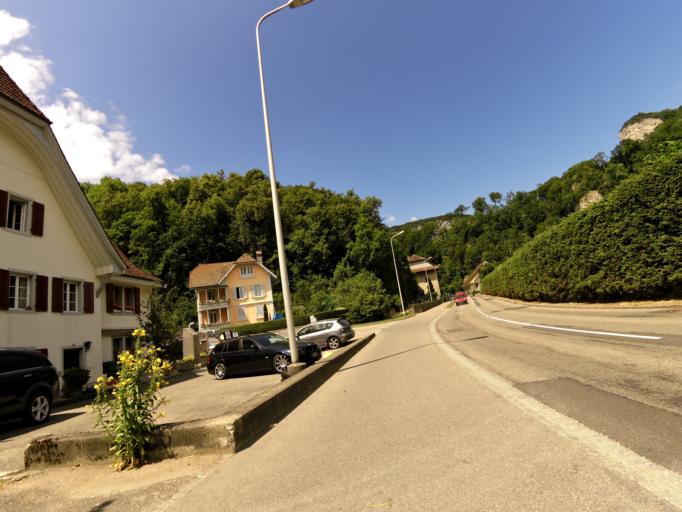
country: CH
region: Solothurn
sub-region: Bezirk Gaeu
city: Oensingen
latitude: 47.2947
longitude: 7.7045
